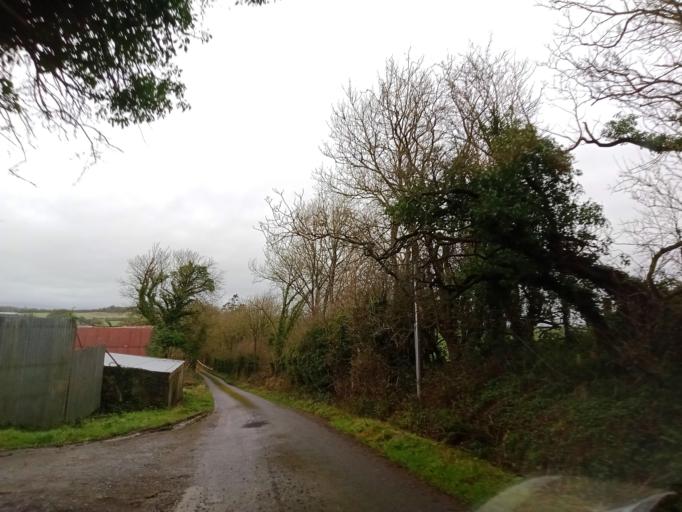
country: IE
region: Munster
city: Fethard
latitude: 52.5584
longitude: -7.7069
